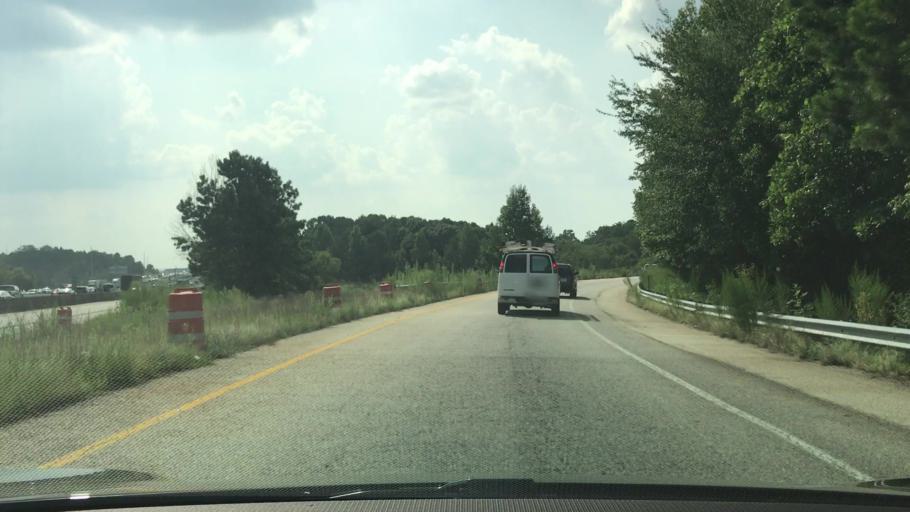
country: US
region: Georgia
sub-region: Gwinnett County
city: Buford
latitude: 34.0578
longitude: -83.9867
